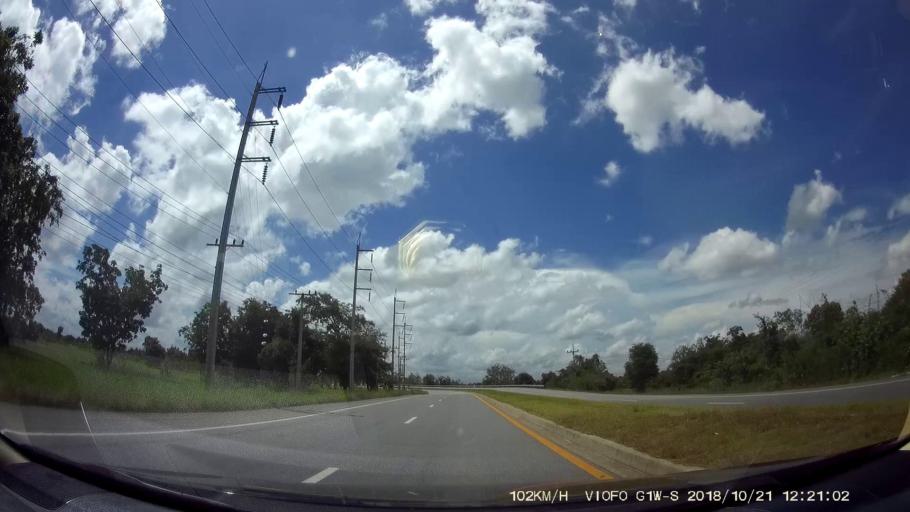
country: TH
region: Nakhon Ratchasima
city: Dan Khun Thot
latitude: 15.2813
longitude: 101.7963
